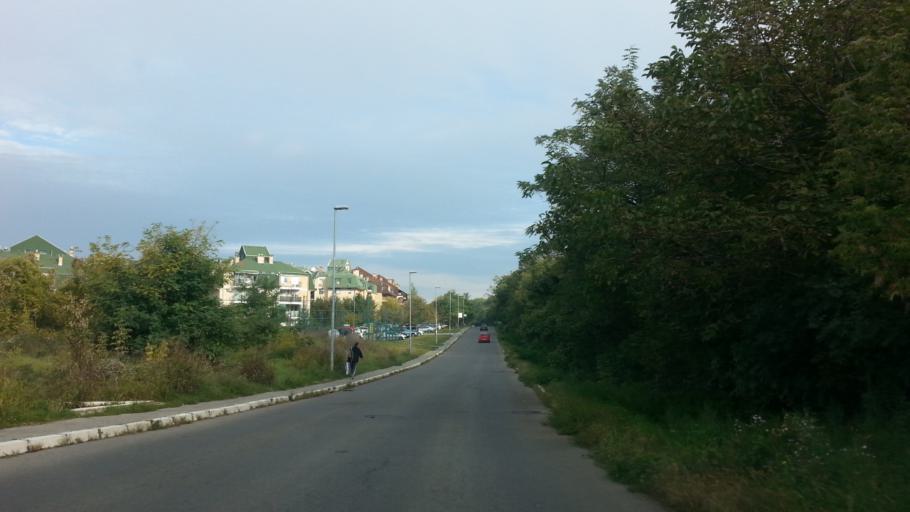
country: RS
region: Central Serbia
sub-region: Belgrade
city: Rakovica
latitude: 44.7524
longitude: 20.4303
